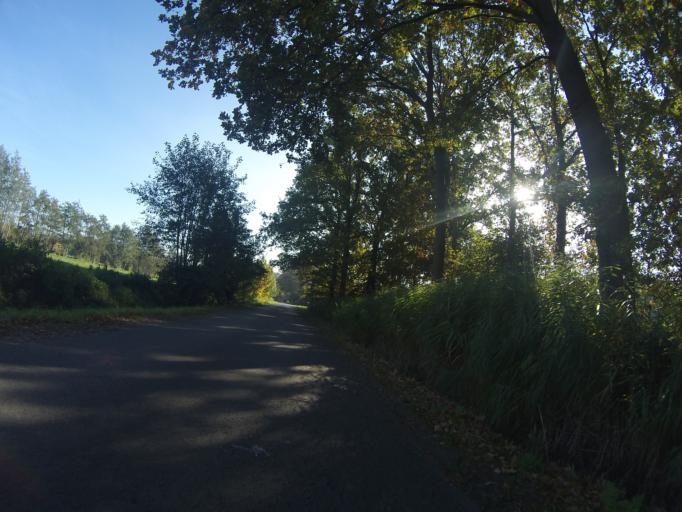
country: NL
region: Gelderland
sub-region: Gemeente Barneveld
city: Terschuur
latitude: 52.1748
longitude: 5.5310
